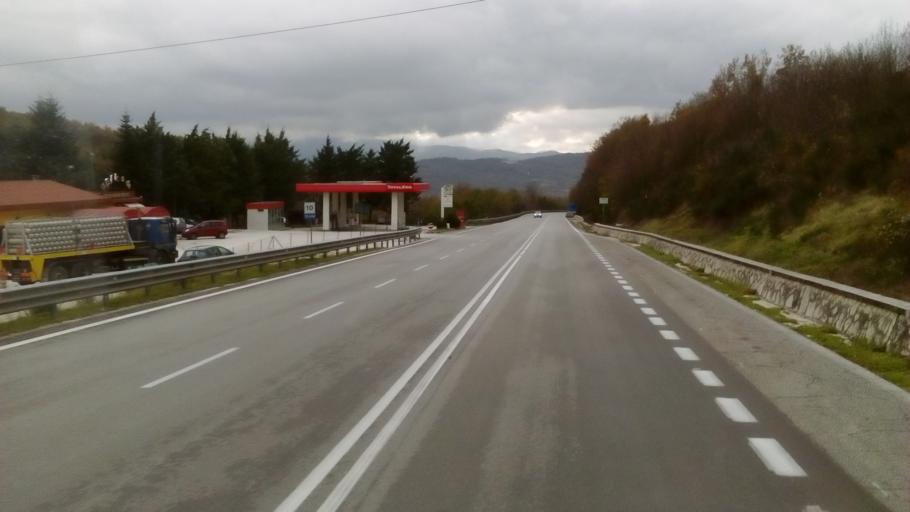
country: IT
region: Molise
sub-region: Provincia di Isernia
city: Sessano del Molise
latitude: 41.6503
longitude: 14.3326
